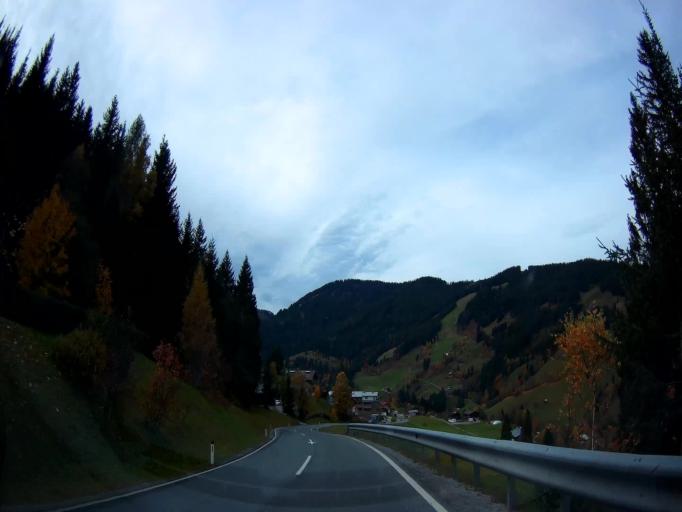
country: AT
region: Salzburg
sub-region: Politischer Bezirk Zell am See
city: Dienten am Hochkonig
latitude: 47.3857
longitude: 13.0193
